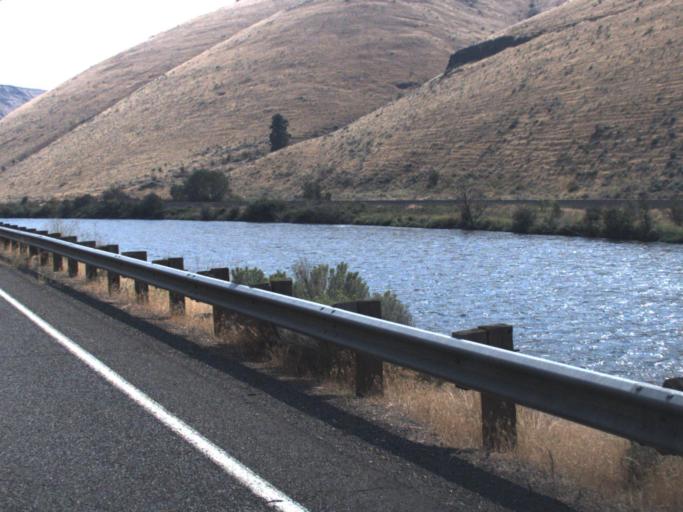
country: US
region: Washington
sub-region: Kittitas County
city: Kittitas
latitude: 46.8740
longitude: -120.4918
